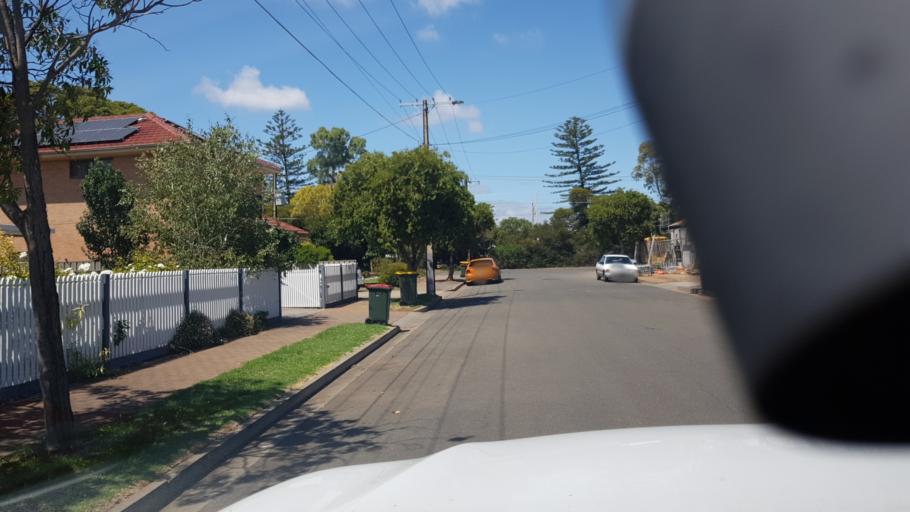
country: AU
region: South Australia
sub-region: Adelaide
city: Brighton
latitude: -35.0106
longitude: 138.5297
